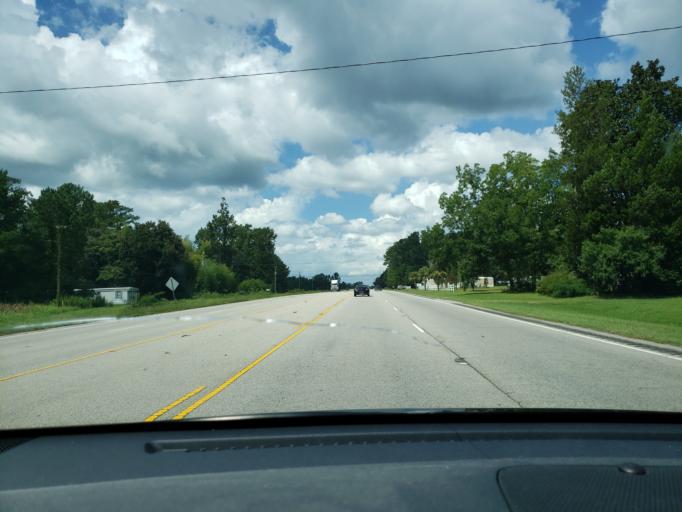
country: US
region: North Carolina
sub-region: Bladen County
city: Elizabethtown
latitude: 34.6655
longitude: -78.7291
